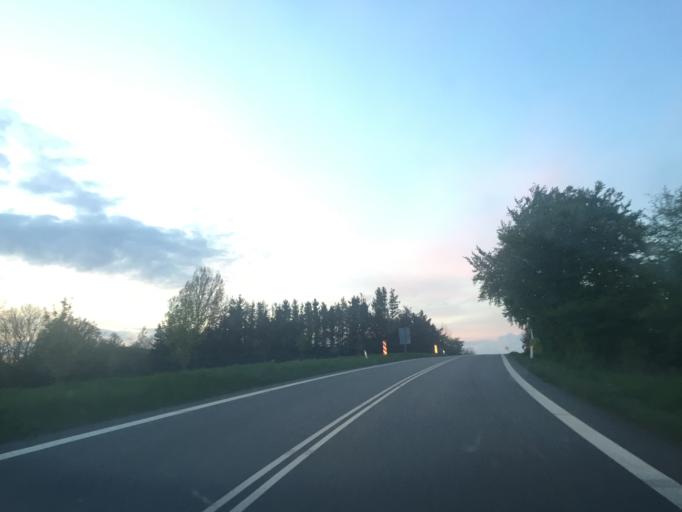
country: DK
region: South Denmark
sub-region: Nyborg Kommune
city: Ullerslev
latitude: 55.2665
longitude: 10.6753
